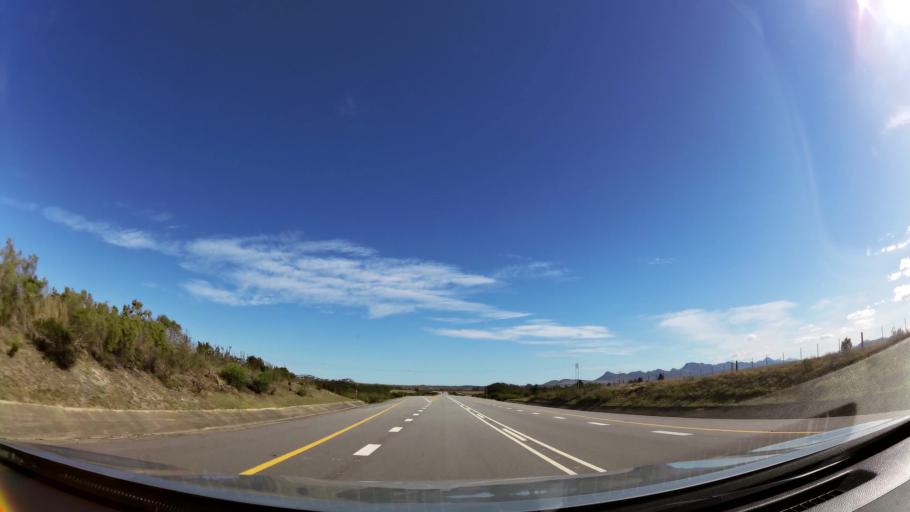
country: ZA
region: Eastern Cape
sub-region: Cacadu District Municipality
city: Kruisfontein
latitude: -34.0264
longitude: 24.6057
